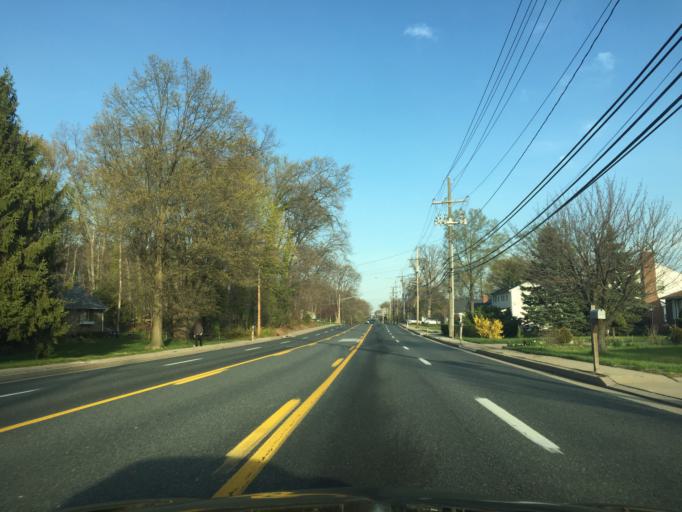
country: US
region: Maryland
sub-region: Baltimore County
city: Perry Hall
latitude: 39.3903
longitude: -76.4816
